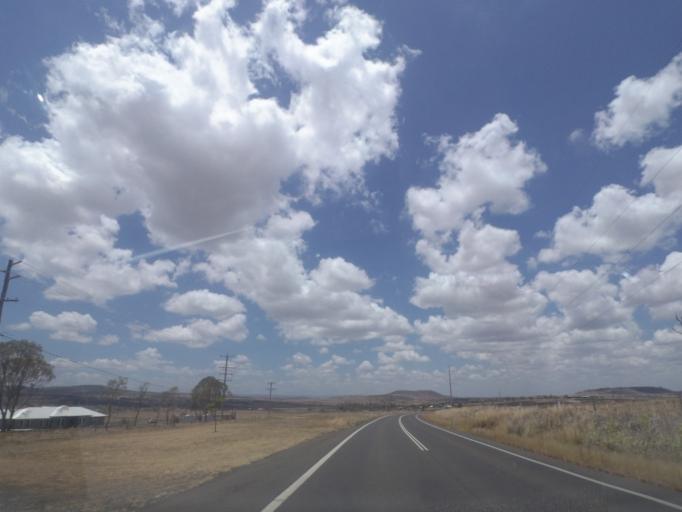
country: AU
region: Queensland
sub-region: Toowoomba
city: Top Camp
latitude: -27.7518
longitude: 151.9342
